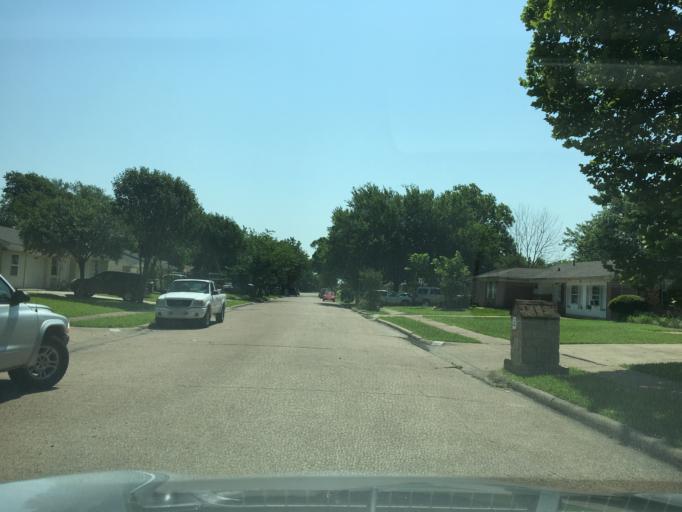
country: US
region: Texas
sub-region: Dallas County
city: Richardson
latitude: 32.9178
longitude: -96.6953
